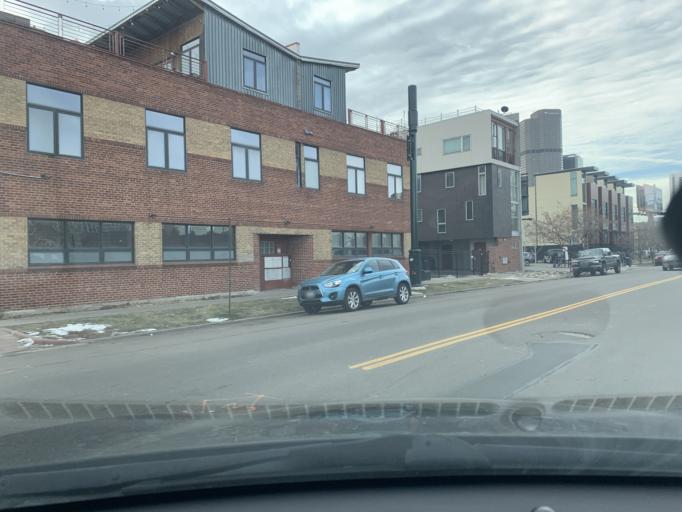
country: US
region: Colorado
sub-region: Denver County
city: Denver
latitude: 39.7546
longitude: -104.9852
